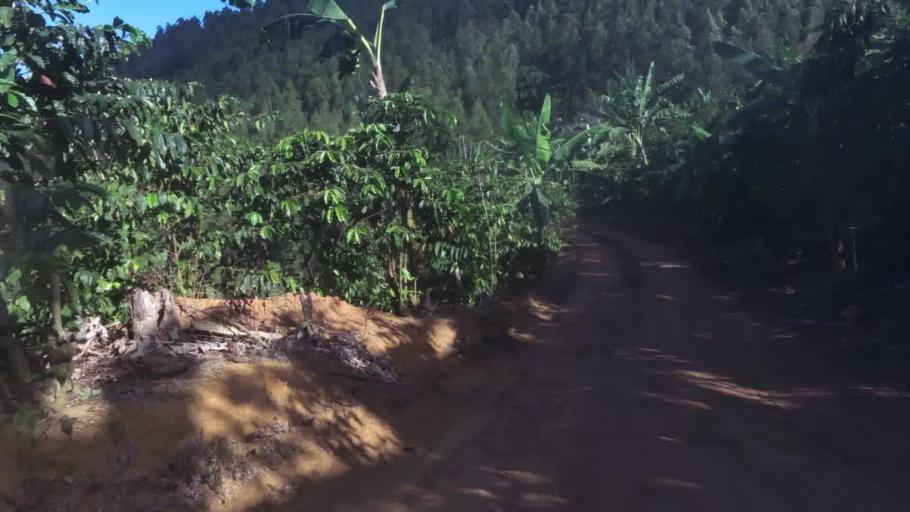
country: BR
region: Espirito Santo
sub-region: Iconha
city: Iconha
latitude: -20.7512
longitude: -40.8059
